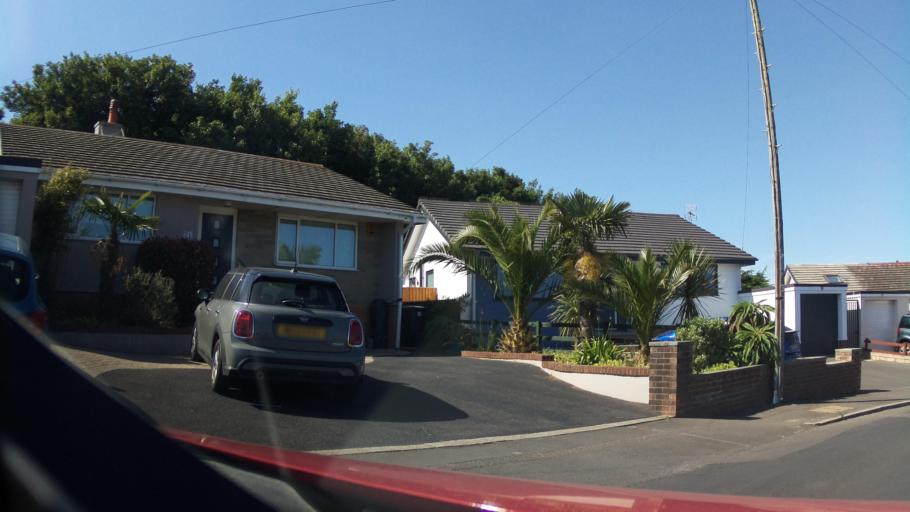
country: GB
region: England
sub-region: Borough of Torbay
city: Brixham
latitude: 50.3998
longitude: -3.5237
